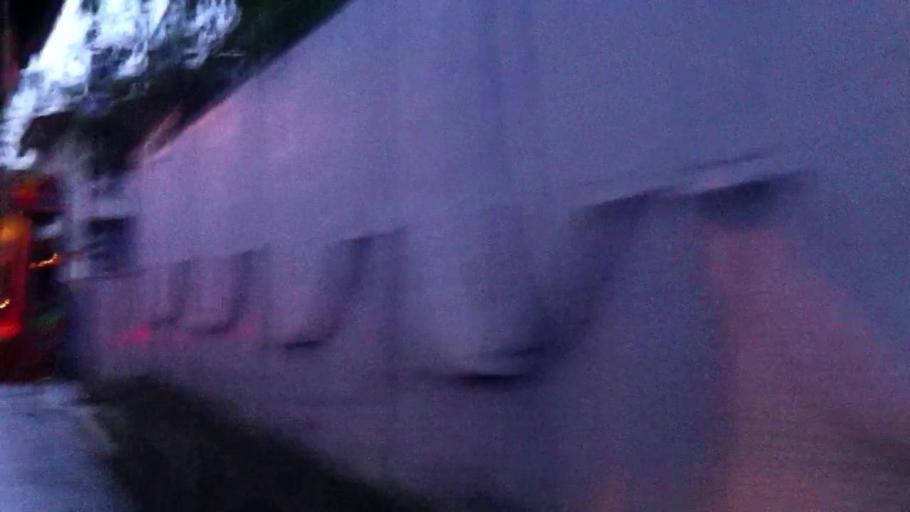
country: PH
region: Cordillera
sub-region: Province of Benguet
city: La Trinidad
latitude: 16.4616
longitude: 120.5872
